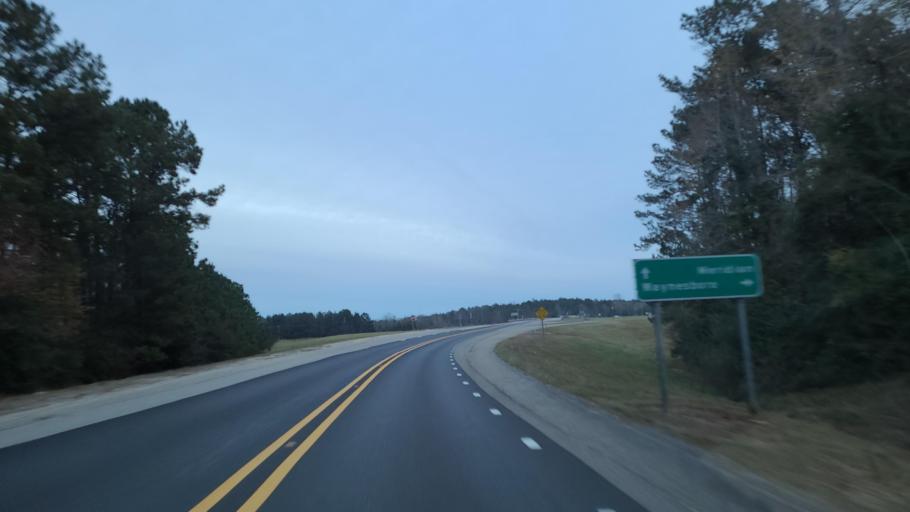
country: US
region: Mississippi
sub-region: Clarke County
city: Quitman
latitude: 32.0583
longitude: -88.6815
